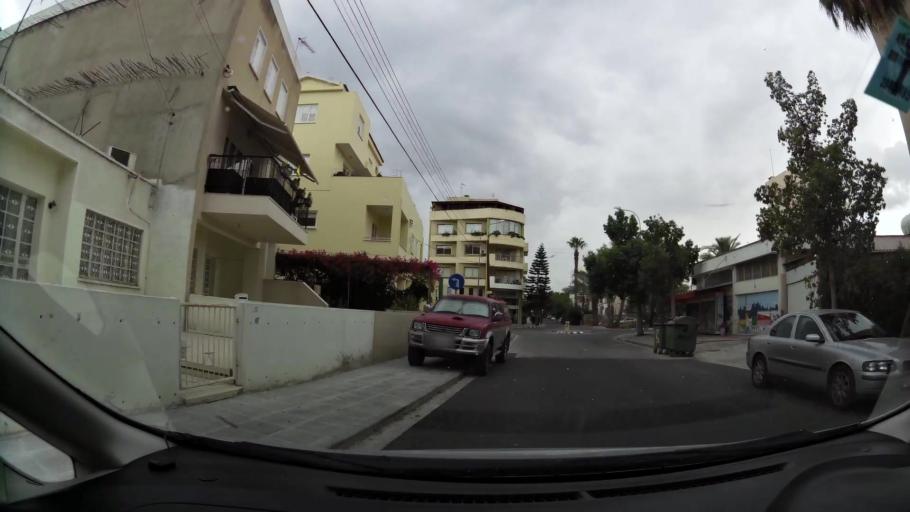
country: CY
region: Lefkosia
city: Nicosia
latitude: 35.1562
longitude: 33.3572
